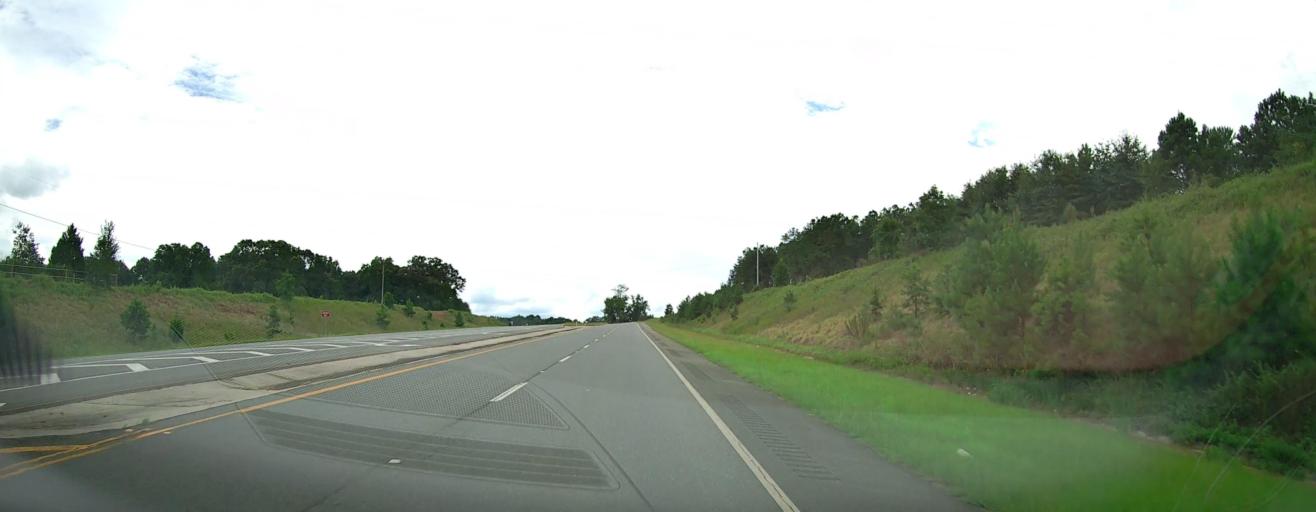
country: US
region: Georgia
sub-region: Schley County
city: Ellaville
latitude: 32.2602
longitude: -84.3042
